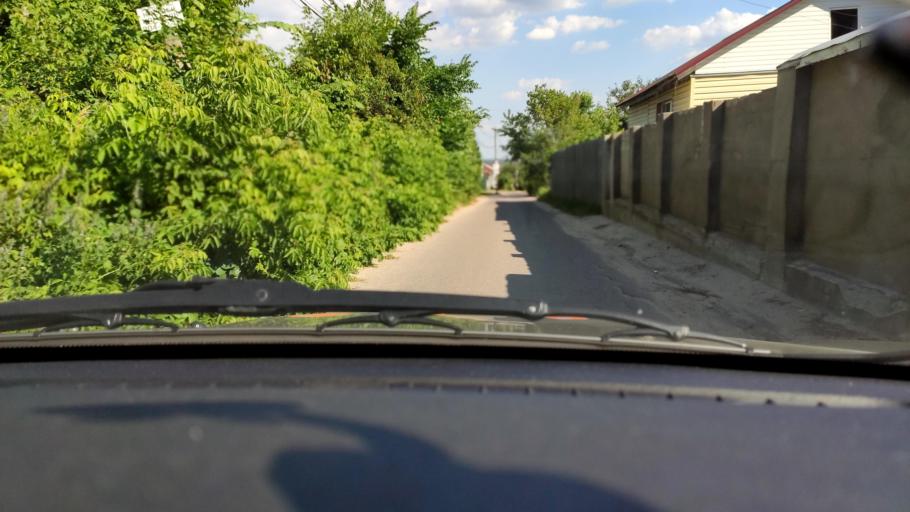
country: RU
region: Voronezj
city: Ramon'
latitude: 51.8238
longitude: 39.2736
